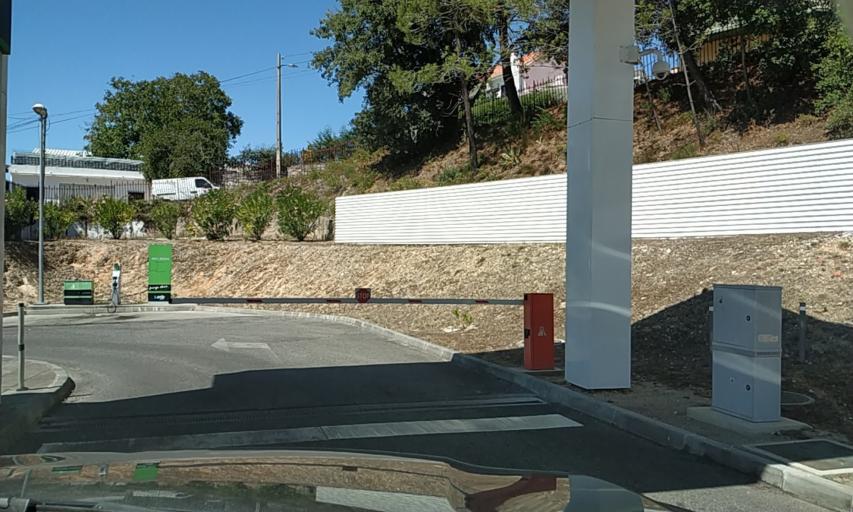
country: PT
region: Leiria
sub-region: Leiria
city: Leiria
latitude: 39.7613
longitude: -8.8203
